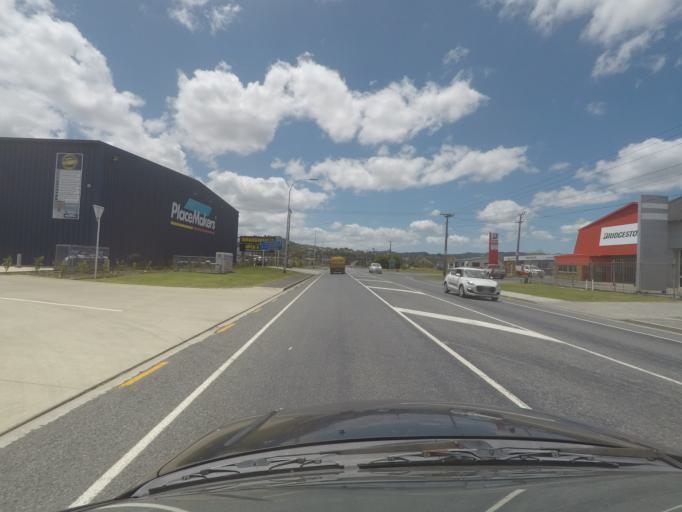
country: NZ
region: Northland
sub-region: Whangarei
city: Whangarei
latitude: -35.7404
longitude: 174.3331
